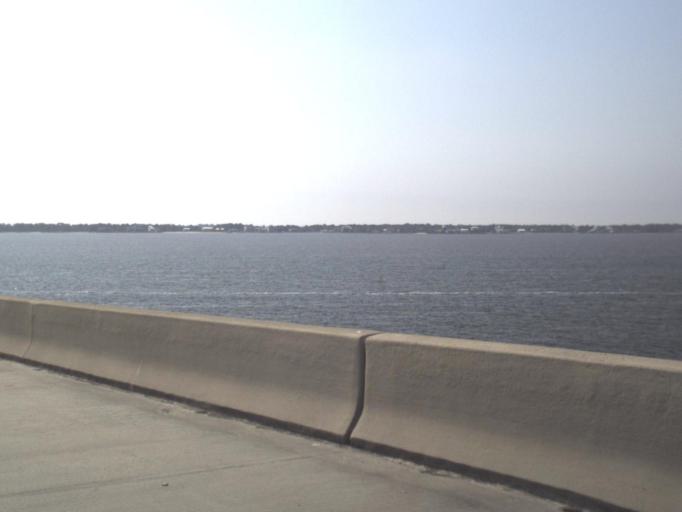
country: US
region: Florida
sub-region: Franklin County
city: Eastpoint
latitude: 29.6811
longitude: -84.8776
